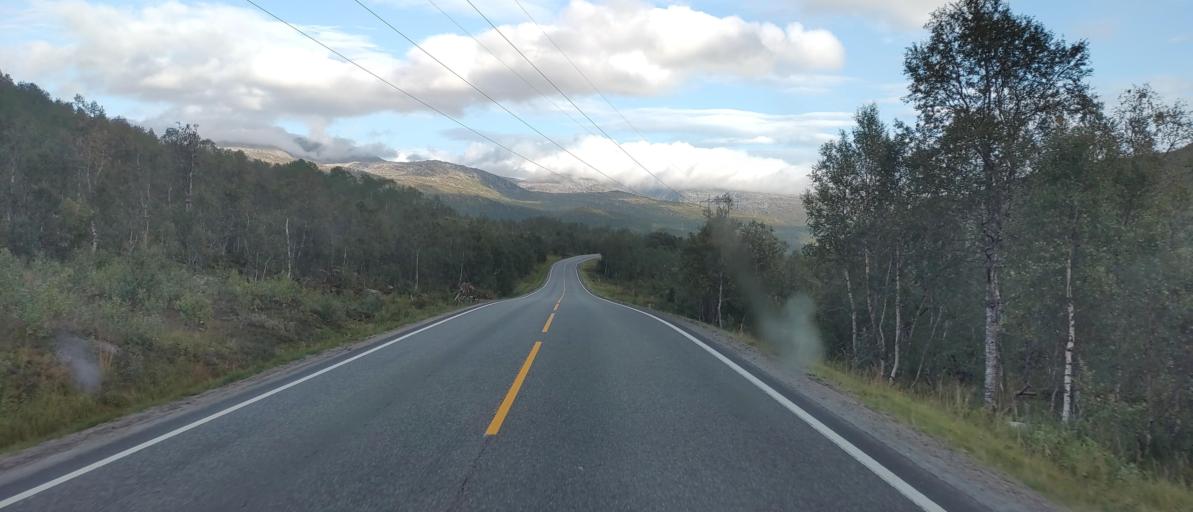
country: NO
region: Nordland
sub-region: Lodingen
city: Lodingen
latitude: 68.5269
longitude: 15.8252
